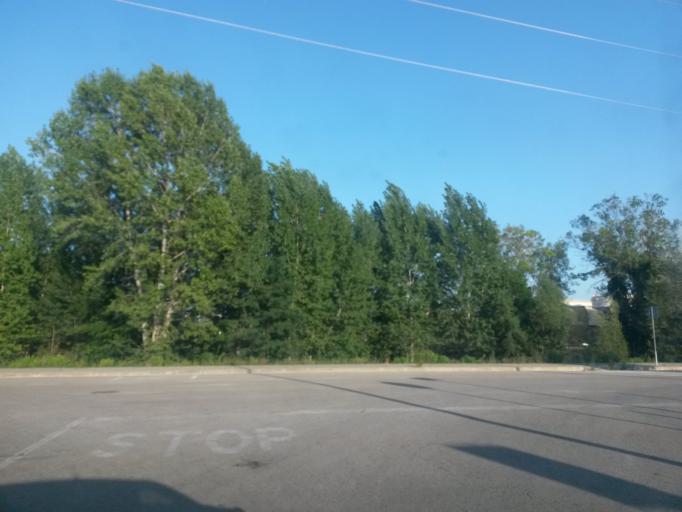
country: ES
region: Catalonia
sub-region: Provincia de Girona
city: Fornells de la Selva
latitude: 41.9499
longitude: 2.8018
